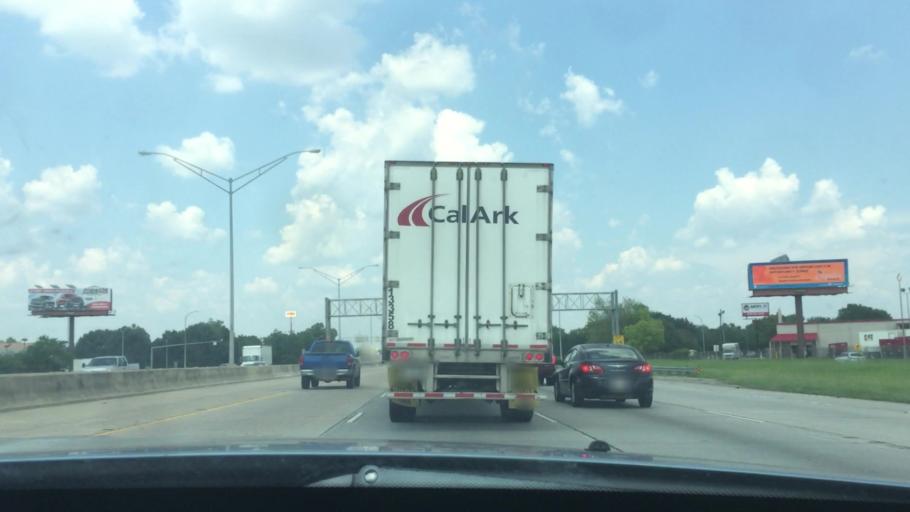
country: US
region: Louisiana
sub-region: East Baton Rouge Parish
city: Westminster
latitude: 30.4217
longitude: -91.0798
